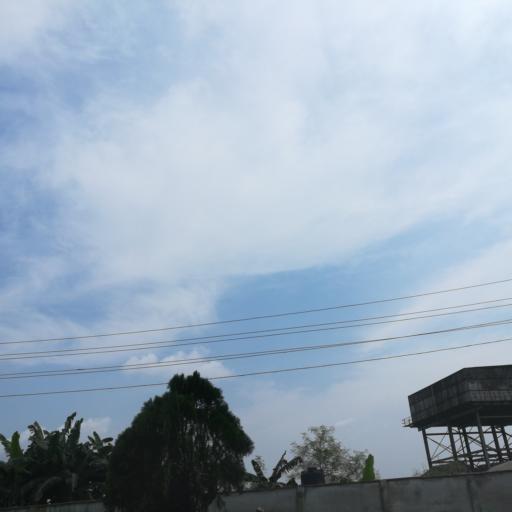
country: NG
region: Rivers
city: Port Harcourt
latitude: 4.8527
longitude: 7.0190
